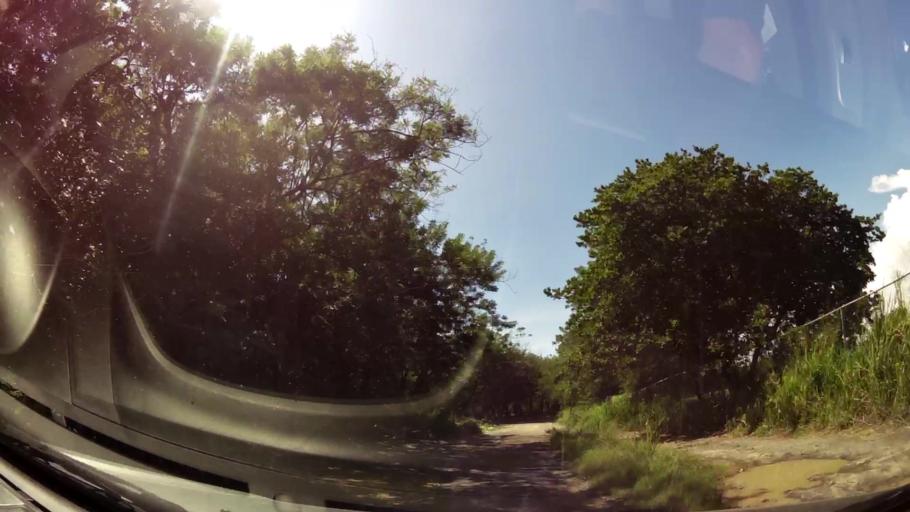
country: PA
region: Panama
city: Nueva Gorgona
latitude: 8.5570
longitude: -79.8591
